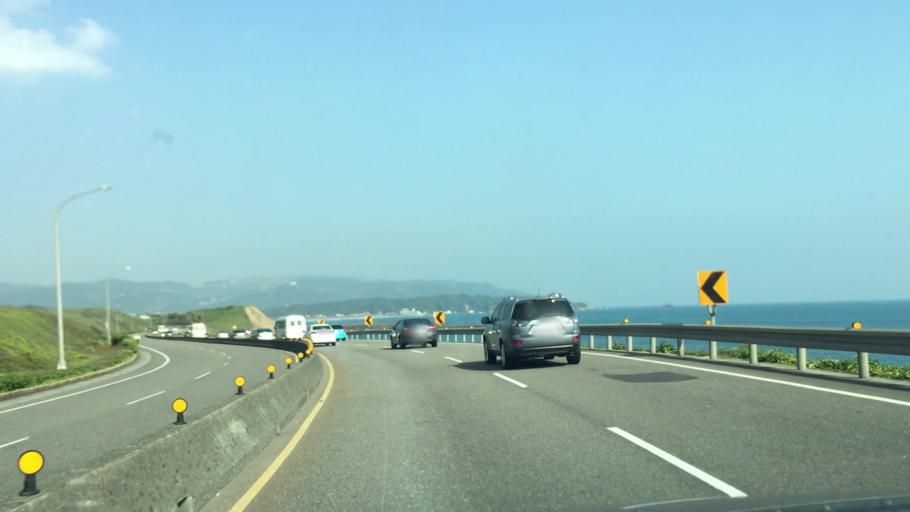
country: TW
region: Taiwan
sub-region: Keelung
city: Keelung
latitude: 25.2021
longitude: 121.6705
